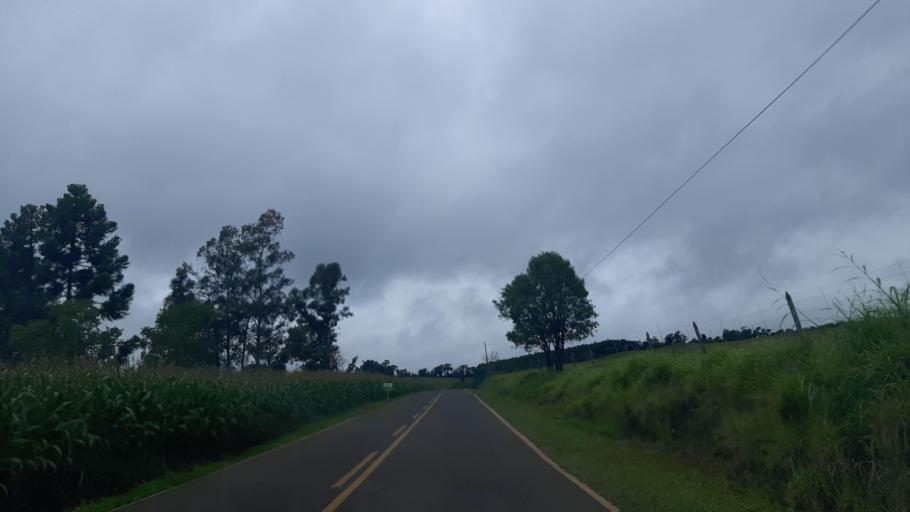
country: BR
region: Parana
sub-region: Ampere
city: Ampere
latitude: -25.9794
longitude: -53.4436
